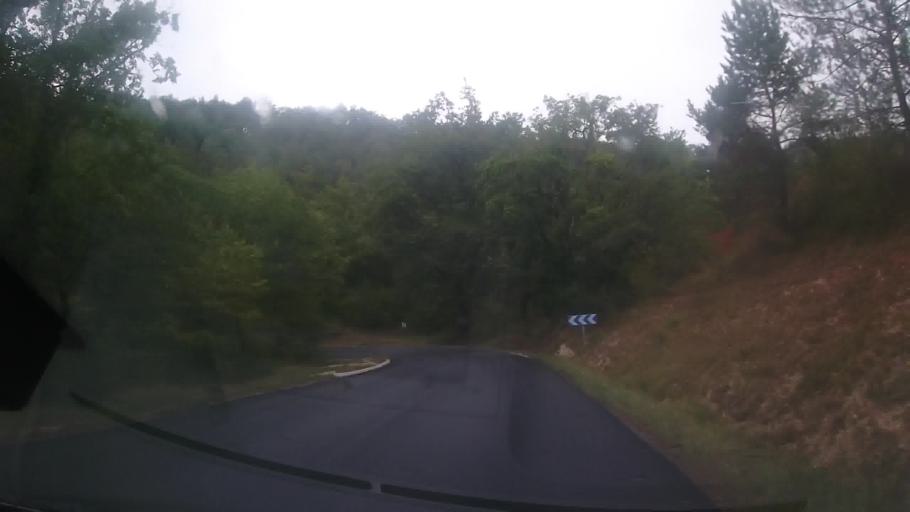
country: FR
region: Aquitaine
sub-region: Departement de la Dordogne
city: Cenac-et-Saint-Julien
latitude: 44.7899
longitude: 1.1833
